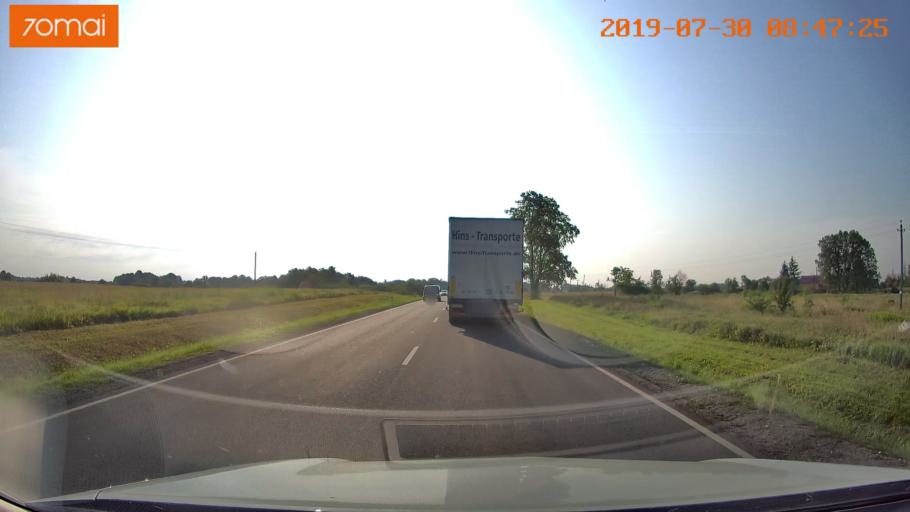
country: RU
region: Kaliningrad
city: Chernyakhovsk
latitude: 54.6214
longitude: 21.8937
